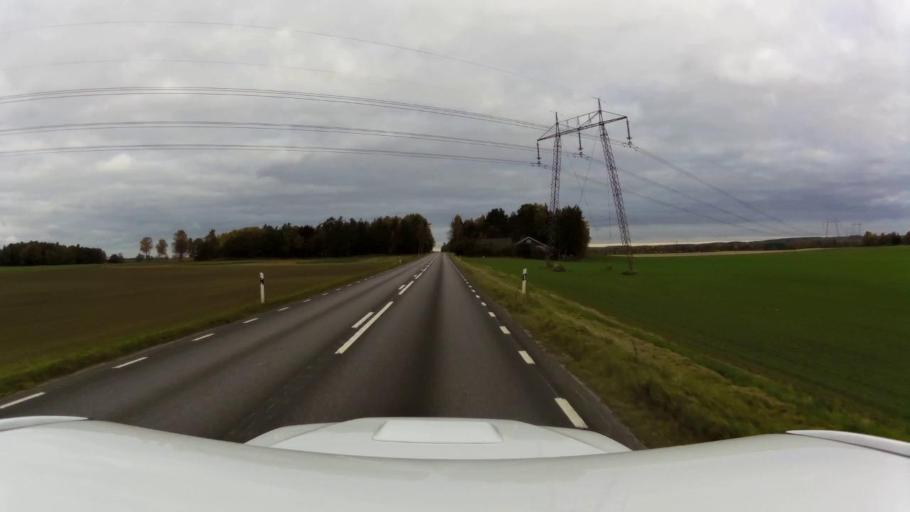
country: SE
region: OEstergoetland
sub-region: Linkopings Kommun
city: Ljungsbro
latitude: 58.5044
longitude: 15.4524
